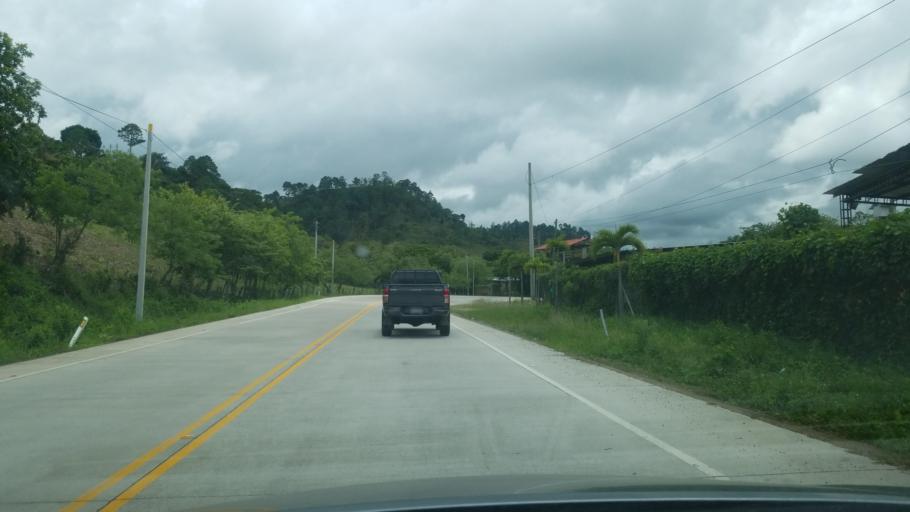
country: HN
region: Copan
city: San Jeronimo
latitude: 14.9852
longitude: -88.8657
